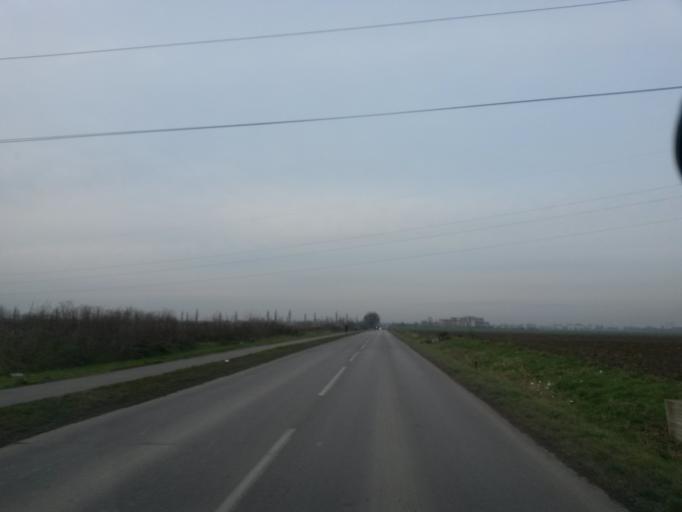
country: HR
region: Osjecko-Baranjska
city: Tenja
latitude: 45.5230
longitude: 18.7257
